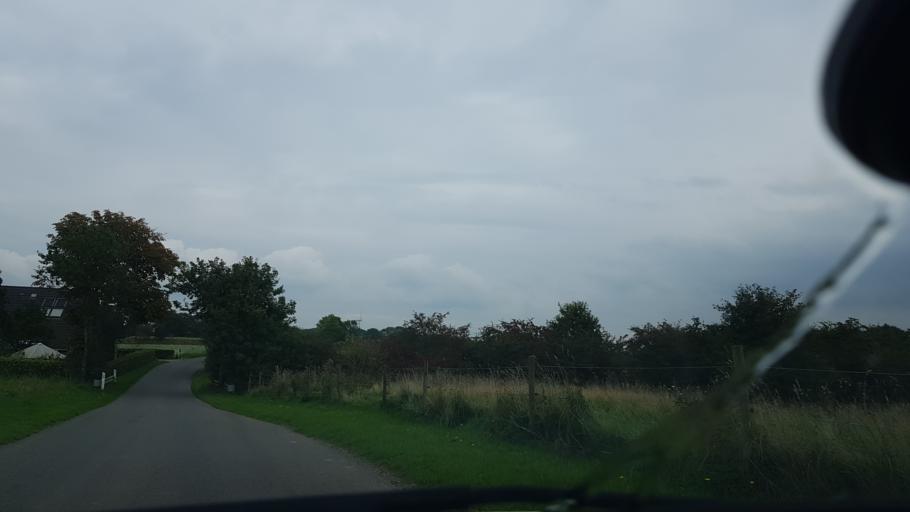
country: DK
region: South Denmark
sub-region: Vejle Kommune
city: Egtved
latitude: 55.5722
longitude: 9.2822
